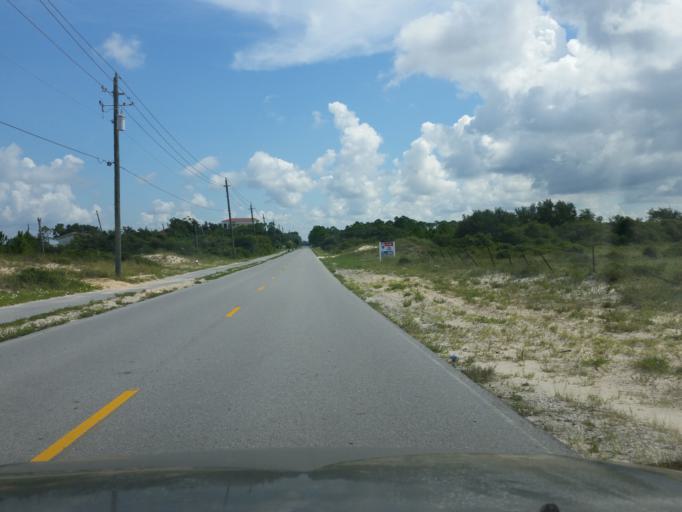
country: US
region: Alabama
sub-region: Baldwin County
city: Orange Beach
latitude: 30.2952
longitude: -87.4514
